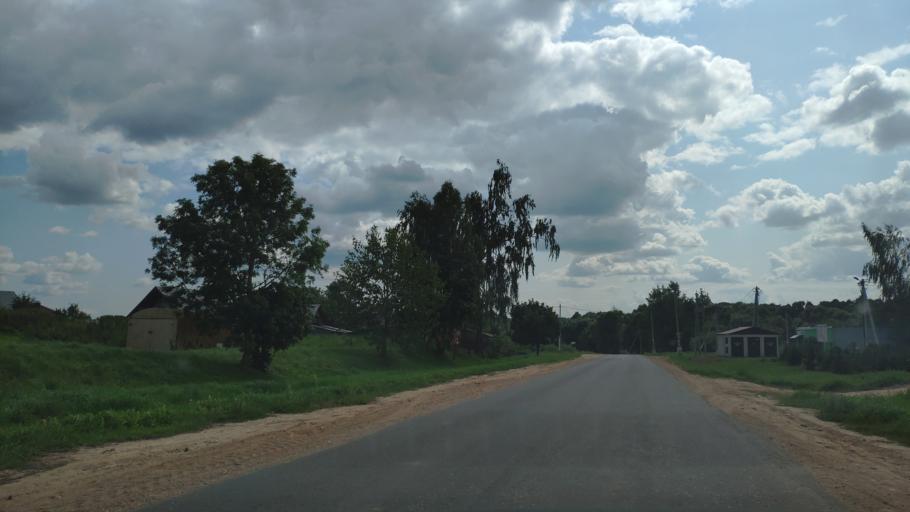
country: BY
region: Minsk
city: Khatsyezhyna
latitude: 53.8691
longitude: 27.3182
